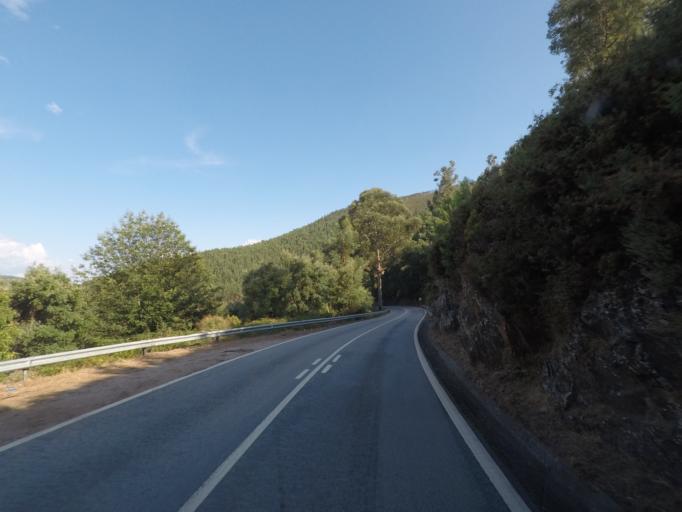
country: PT
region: Vila Real
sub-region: Mesao Frio
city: Mesao Frio
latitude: 41.1755
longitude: -7.9229
